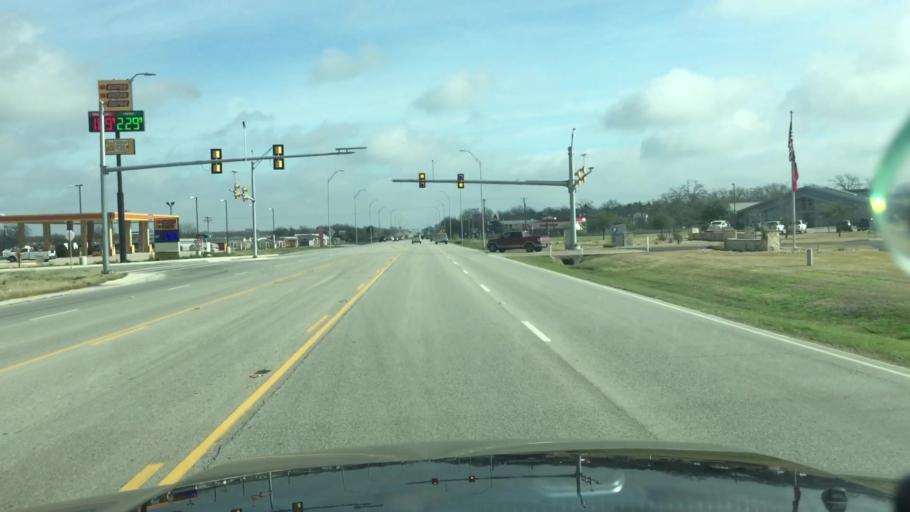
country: US
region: Texas
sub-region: Lee County
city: Giddings
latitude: 30.1783
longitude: -96.9081
